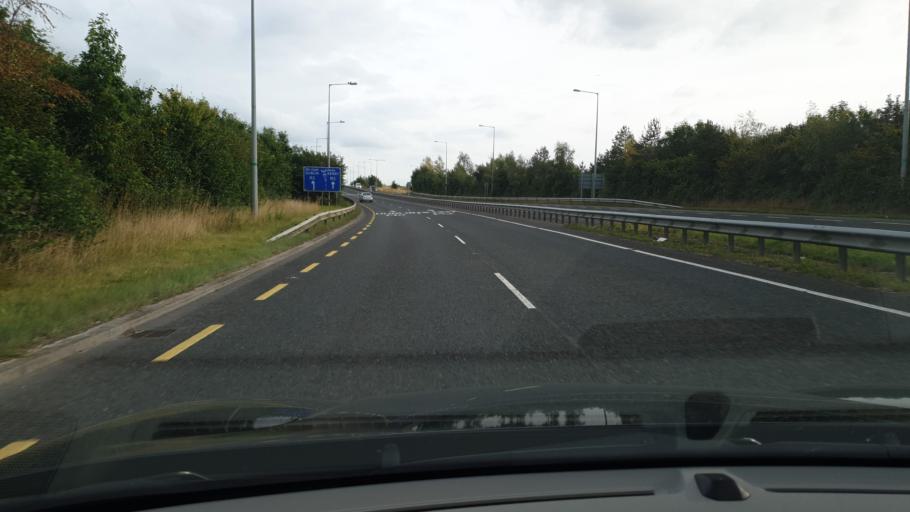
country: IE
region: Leinster
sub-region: An Mhi
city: Ashbourne
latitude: 53.4924
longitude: -6.3864
